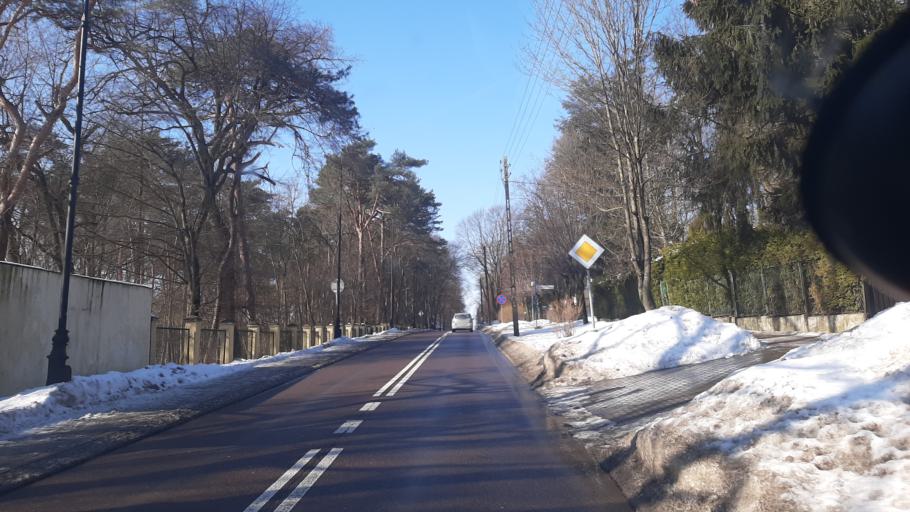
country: PL
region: Lublin Voivodeship
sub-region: Powiat pulawski
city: Naleczow
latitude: 51.2880
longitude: 22.2132
